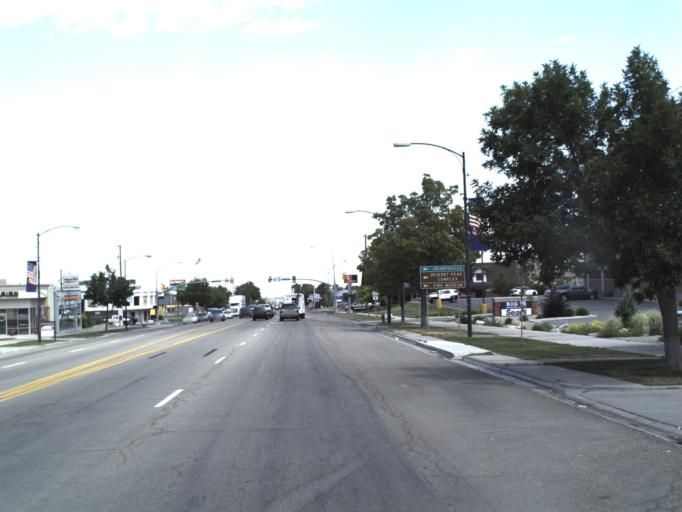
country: US
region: Utah
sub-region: Tooele County
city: Tooele
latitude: 40.5299
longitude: -112.2985
